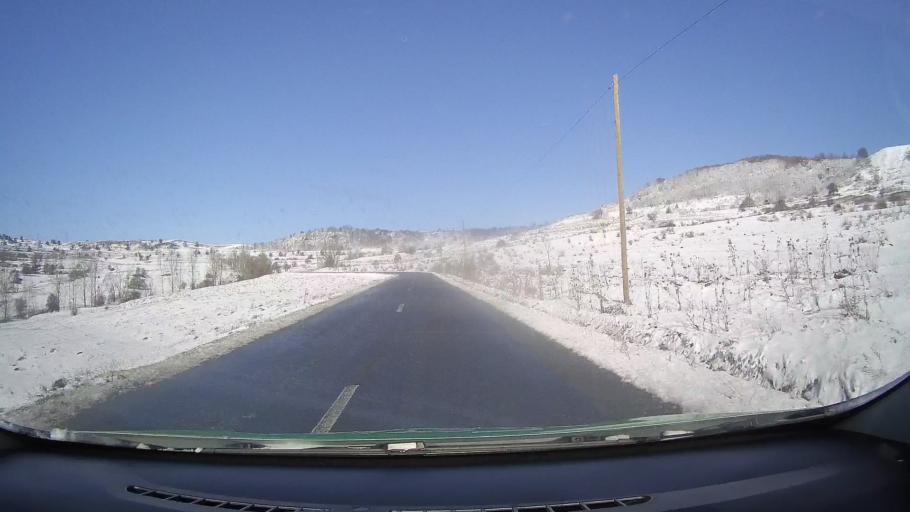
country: RO
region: Sibiu
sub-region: Comuna Avrig
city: Avrig
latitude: 45.7716
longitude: 24.3841
